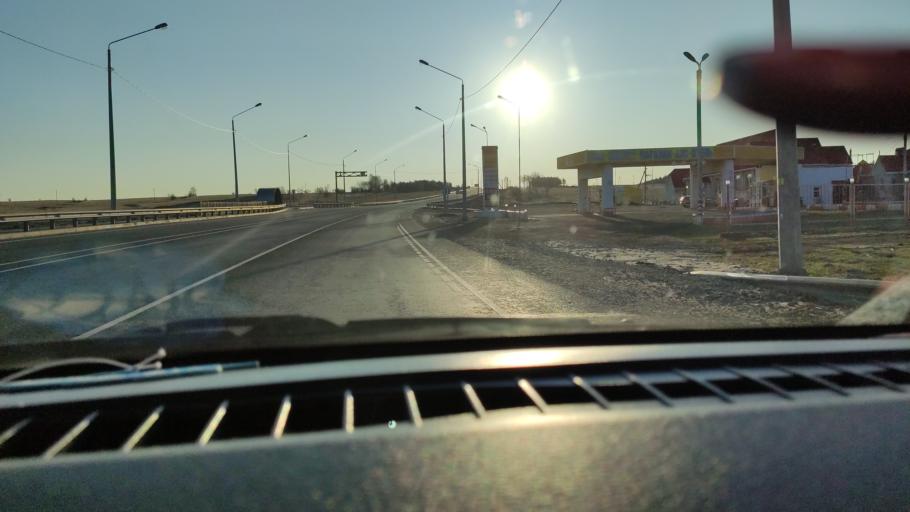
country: RU
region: Saratov
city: Sennoy
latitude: 52.1597
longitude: 47.0823
